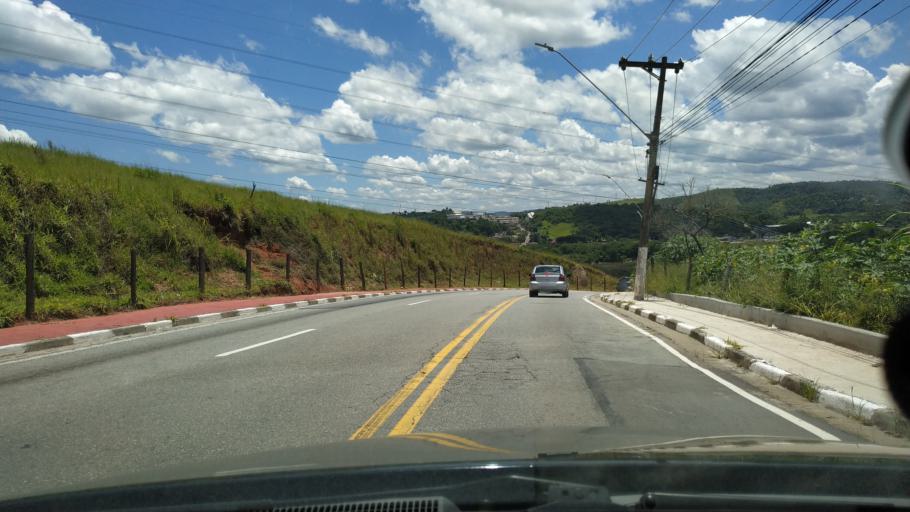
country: BR
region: Sao Paulo
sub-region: Santana De Parnaiba
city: Santana de Parnaiba
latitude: -23.4492
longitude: -46.9063
